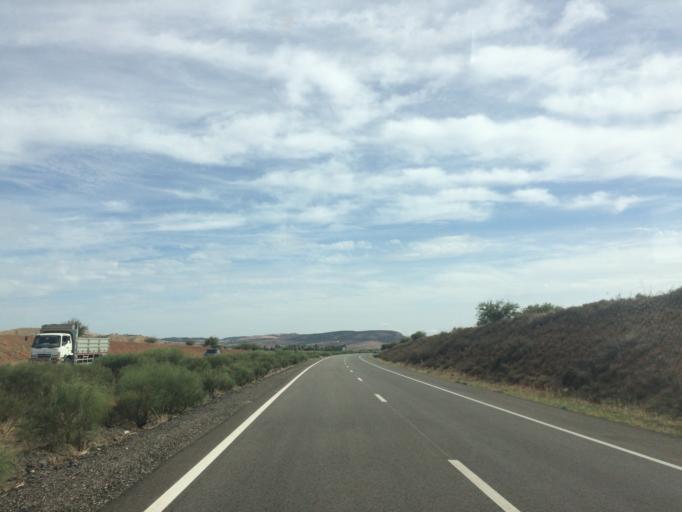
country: MA
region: Rabat-Sale-Zemmour-Zaer
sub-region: Khemisset
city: Khemisset
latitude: 33.7825
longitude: -5.9255
